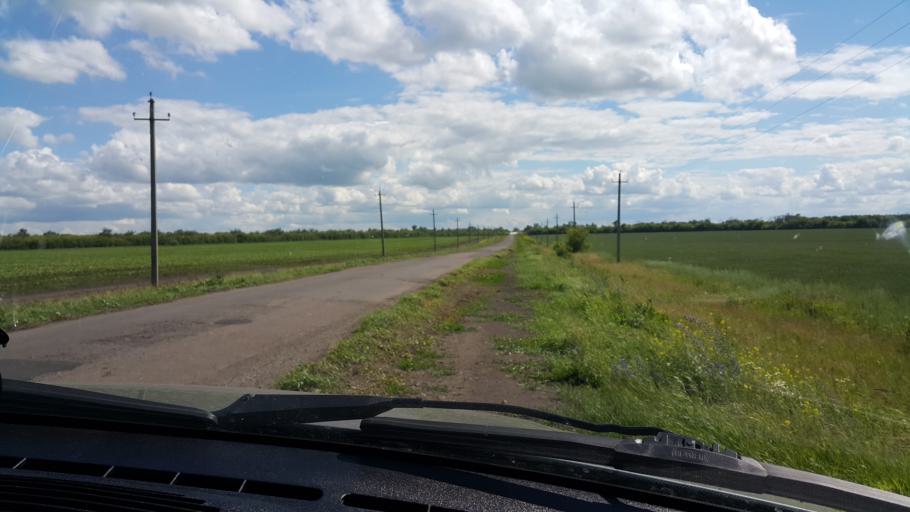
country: RU
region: Tambov
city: Satinka
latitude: 52.3984
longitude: 41.6644
